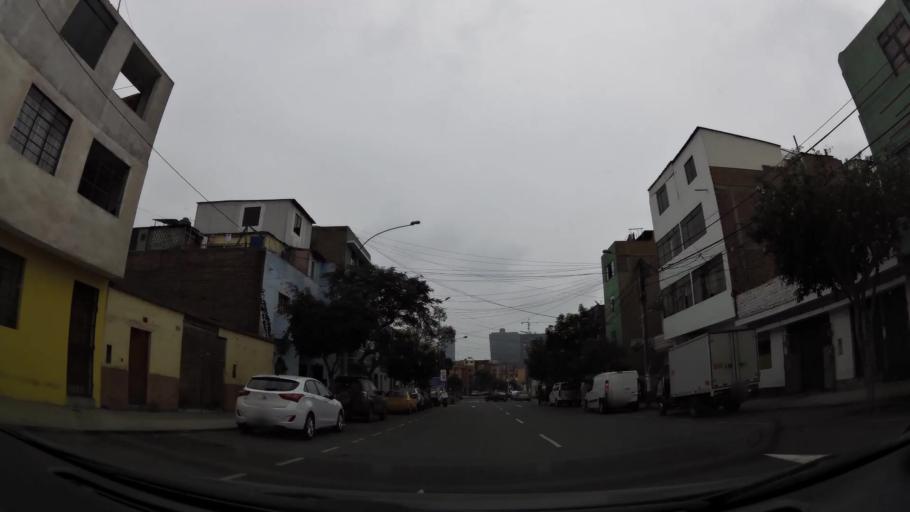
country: PE
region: Lima
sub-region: Lima
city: San Luis
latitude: -12.0857
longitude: -77.0289
